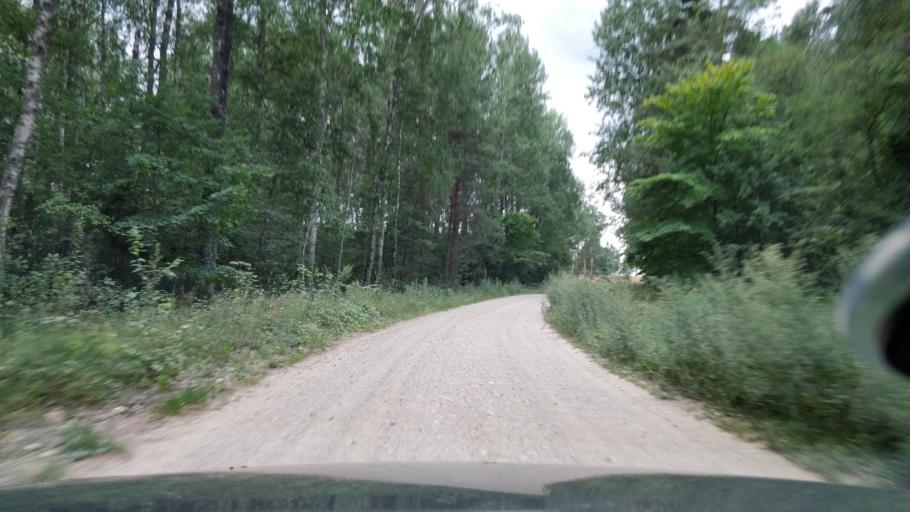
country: LV
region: Ogre
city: Ogre
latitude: 56.7985
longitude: 24.6690
